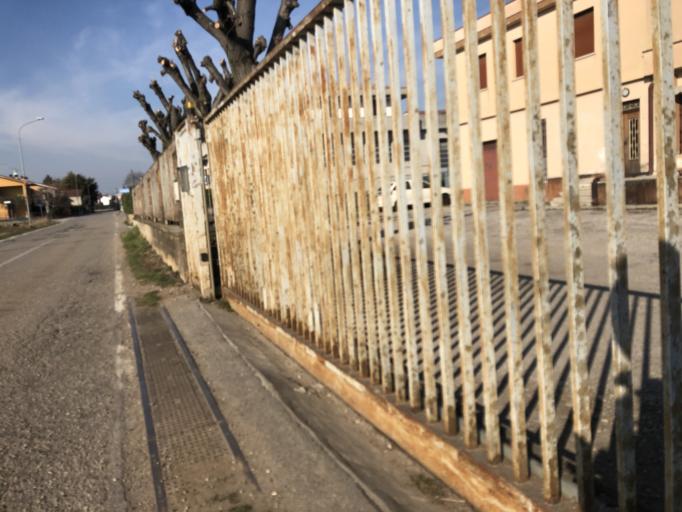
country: IT
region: Veneto
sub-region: Provincia di Verona
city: Lugagnano
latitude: 45.4299
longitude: 10.8812
